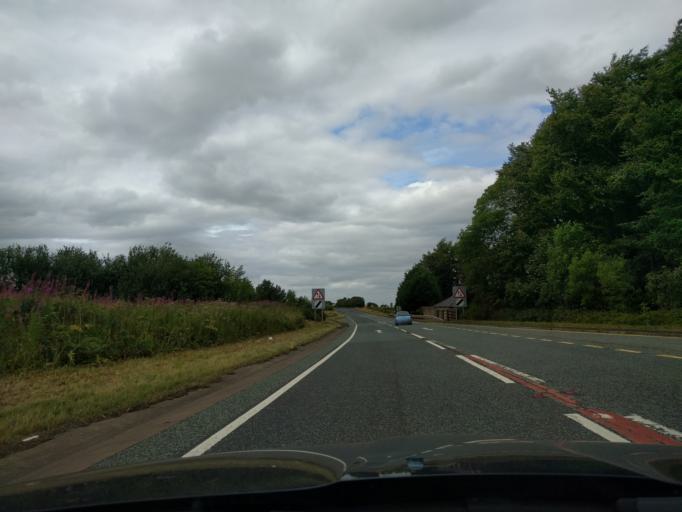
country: GB
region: England
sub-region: Northumberland
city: Ellingham
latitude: 55.5184
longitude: -1.7457
